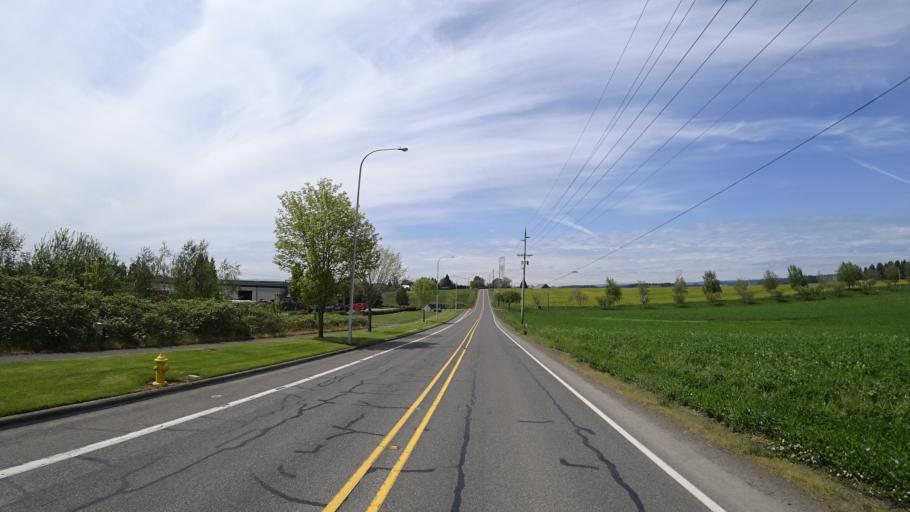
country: US
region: Oregon
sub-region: Washington County
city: Rockcreek
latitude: 45.5739
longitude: -122.9083
